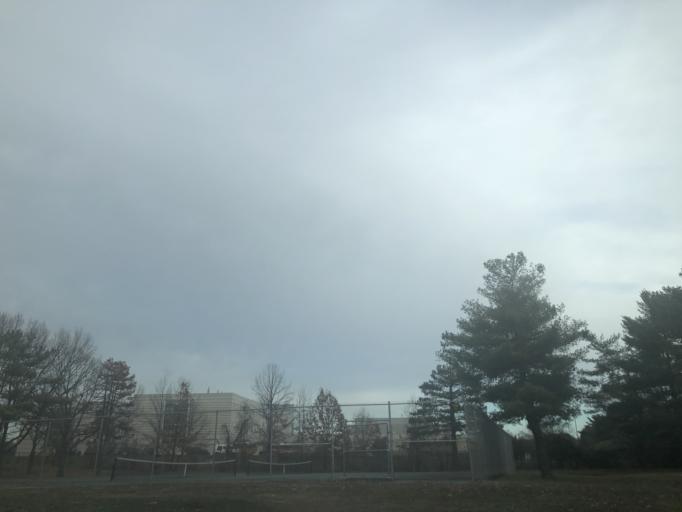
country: US
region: Maryland
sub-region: Prince George's County
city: Oxon Hill
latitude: 38.7958
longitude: -76.9966
